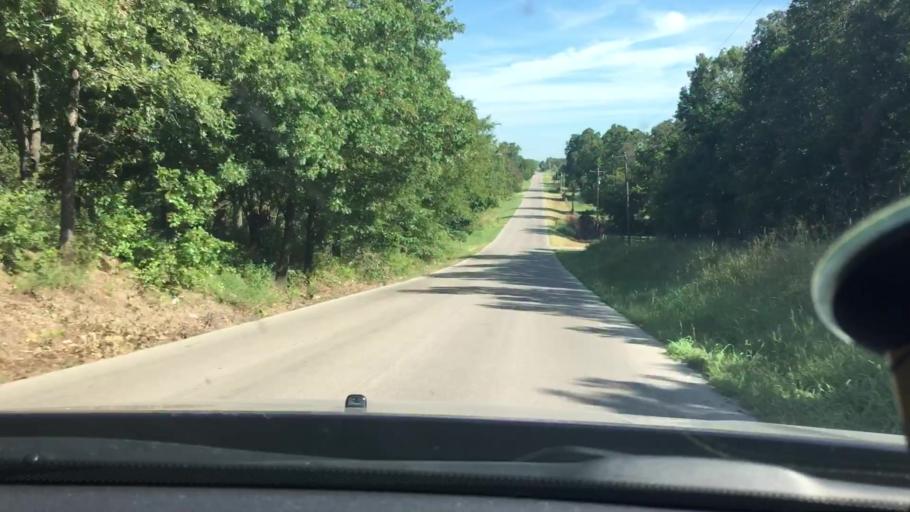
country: US
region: Oklahoma
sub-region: Carter County
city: Lone Grove
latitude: 34.2374
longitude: -97.2474
